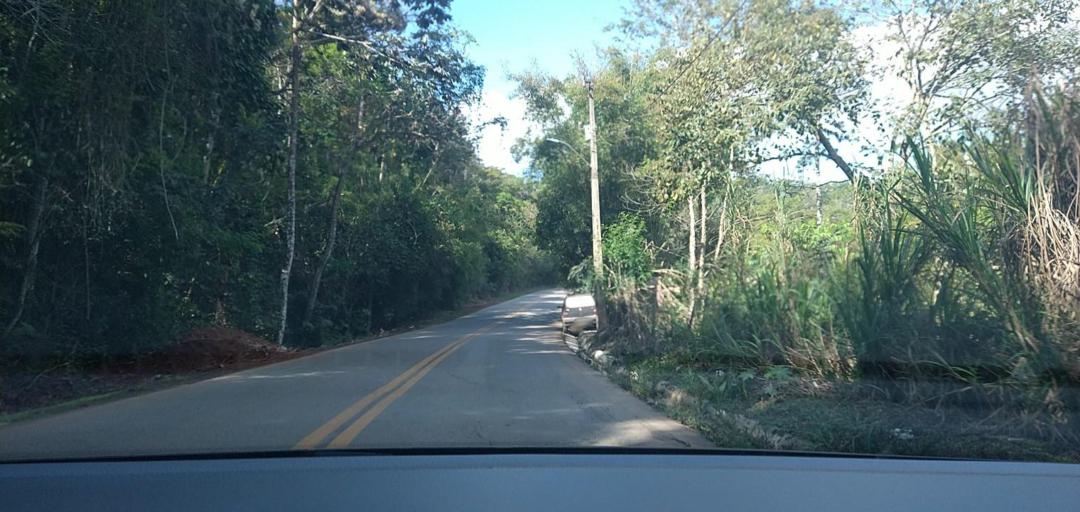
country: BR
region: Minas Gerais
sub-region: Rio Piracicaba
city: Rio Piracicaba
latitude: -19.9518
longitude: -43.1747
